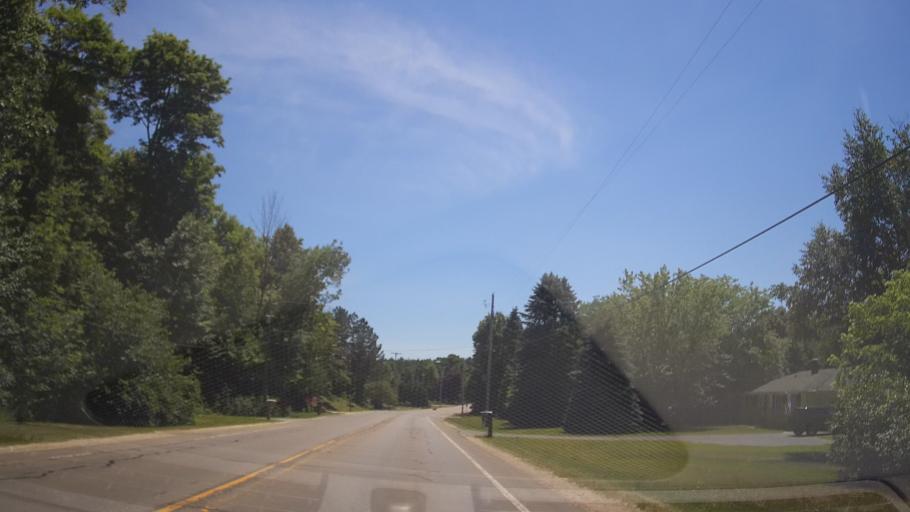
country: US
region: Michigan
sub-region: Grand Traverse County
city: Traverse City
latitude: 44.6882
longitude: -85.6899
